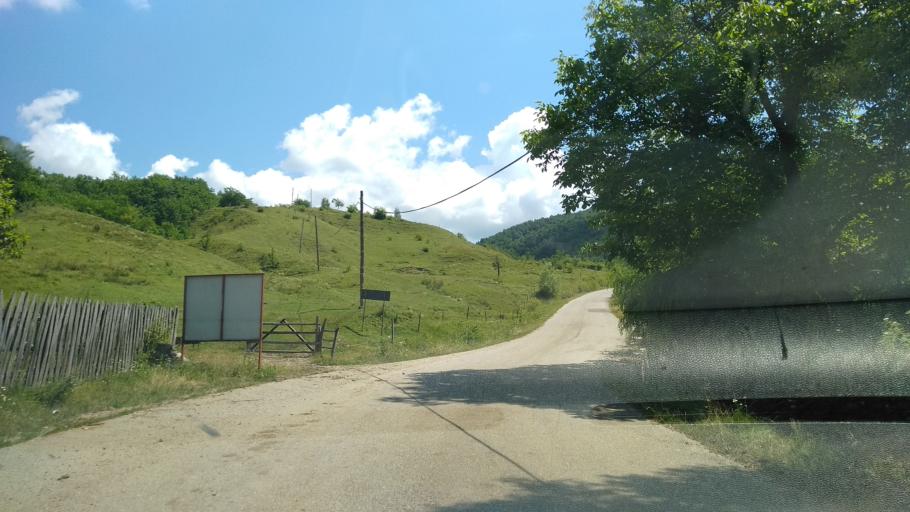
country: RO
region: Hunedoara
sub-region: Comuna Orastioara de Sus
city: Orastioara de Sus
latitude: 45.7082
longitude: 23.1383
